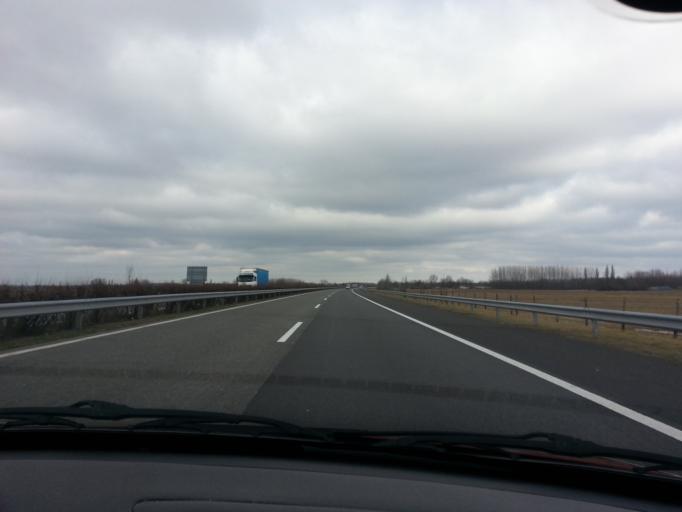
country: HU
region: Csongrad
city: Csengele
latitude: 46.6220
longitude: 19.8347
